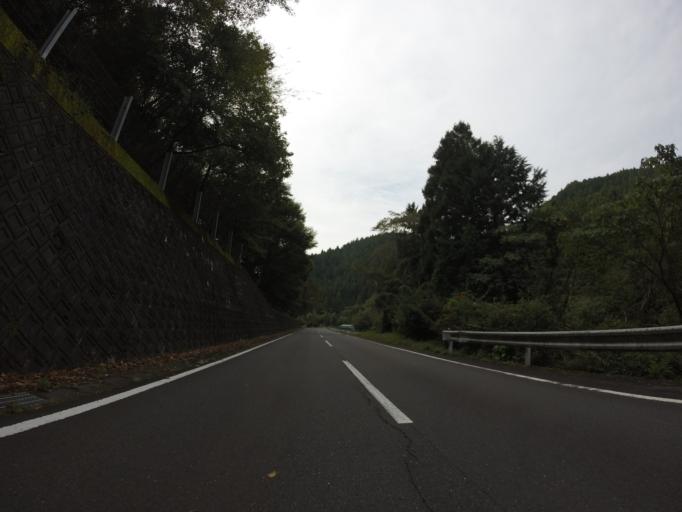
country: JP
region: Shizuoka
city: Kanaya
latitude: 34.8868
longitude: 138.0353
